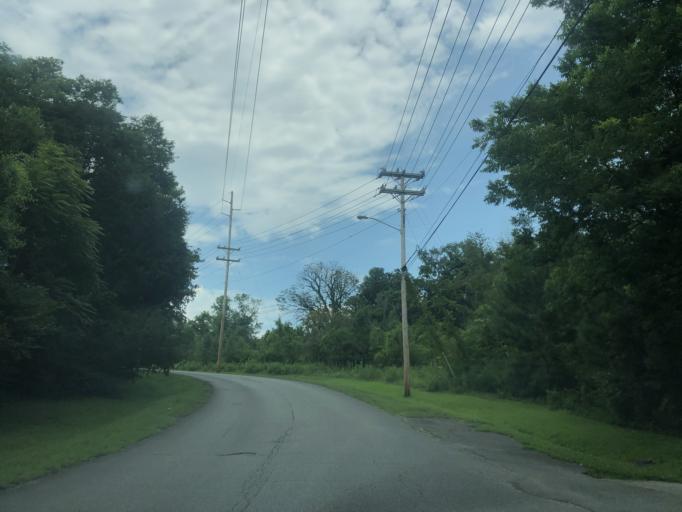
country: US
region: Tennessee
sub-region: Davidson County
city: Oak Hill
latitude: 36.1006
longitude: -86.6707
